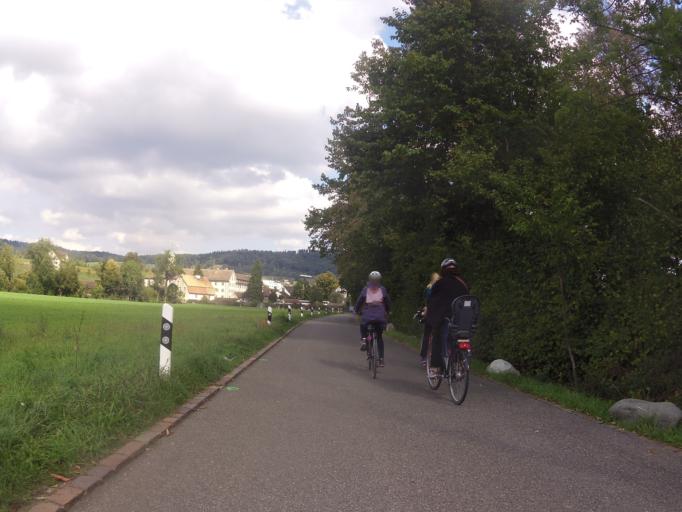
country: CH
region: Zurich
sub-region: Bezirk Dietikon
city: Schlieren / Engstingerquartier
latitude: 47.4057
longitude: 8.4368
